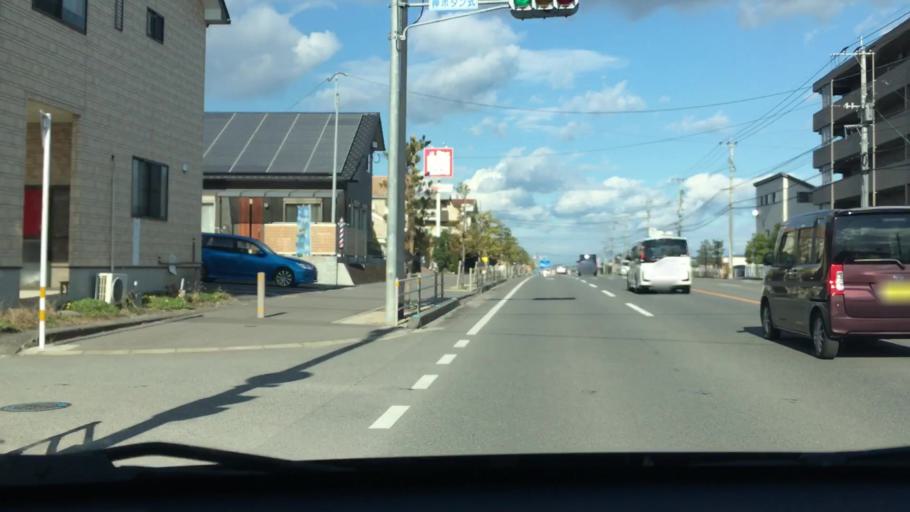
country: JP
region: Oita
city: Tsurusaki
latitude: 33.1845
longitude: 131.6683
